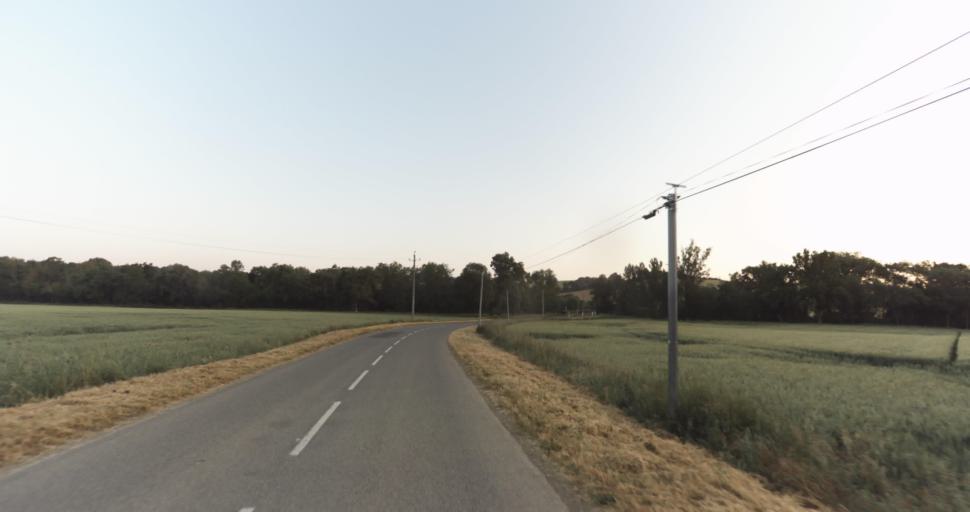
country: FR
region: Midi-Pyrenees
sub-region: Departement de la Haute-Garonne
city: Levignac
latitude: 43.6509
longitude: 1.1507
